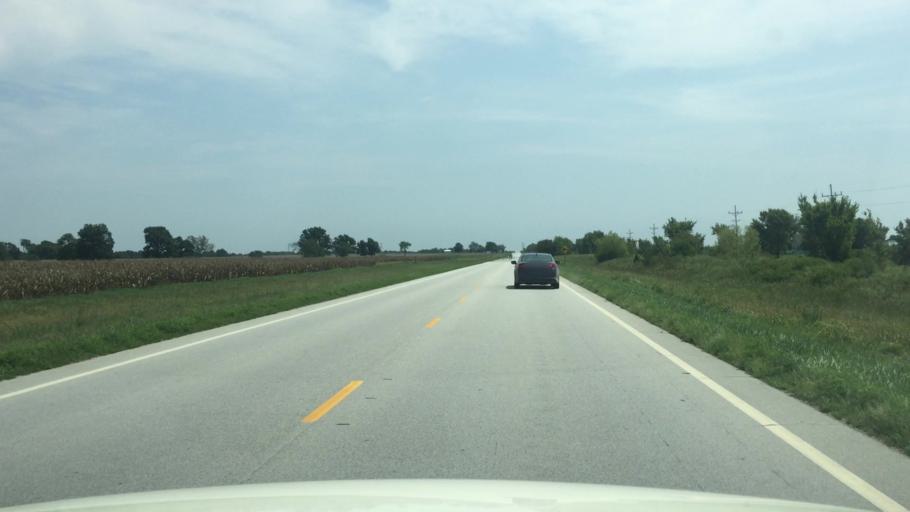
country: US
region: Kansas
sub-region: Cherokee County
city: Columbus
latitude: 37.1792
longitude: -94.9264
